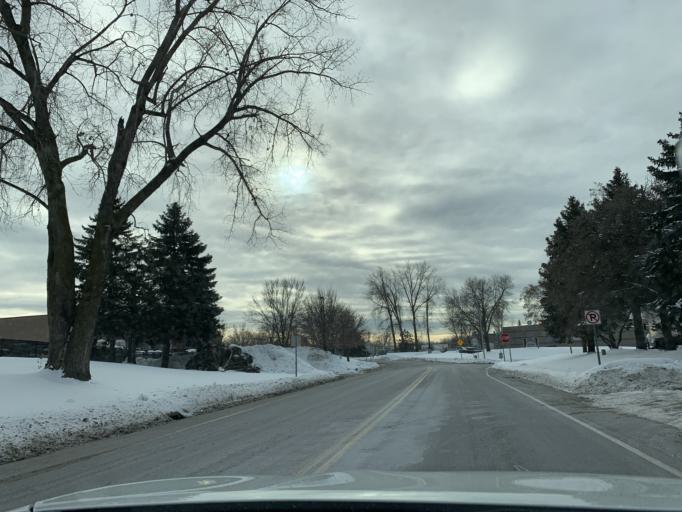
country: US
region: Minnesota
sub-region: Hennepin County
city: West Coon Rapids
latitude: 45.1783
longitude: -93.2981
